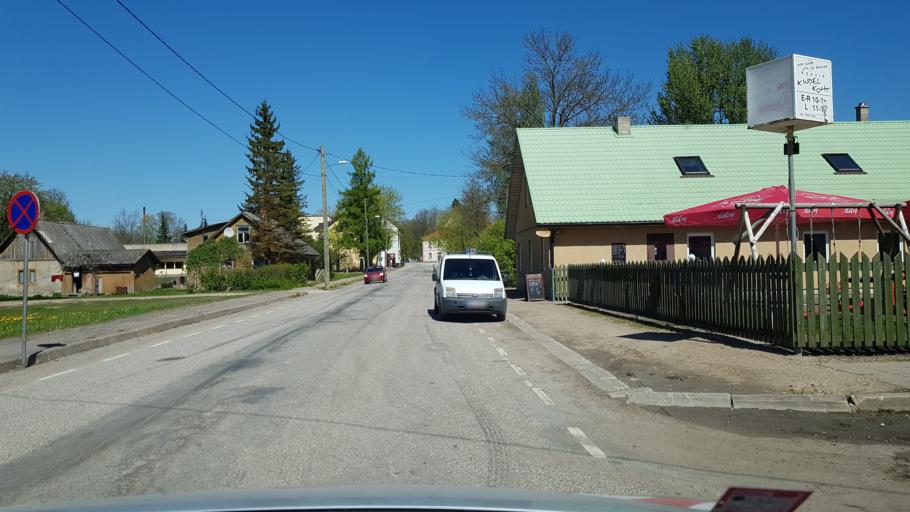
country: EE
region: Vorumaa
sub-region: Antsla vald
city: Vana-Antsla
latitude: 57.8275
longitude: 26.5260
